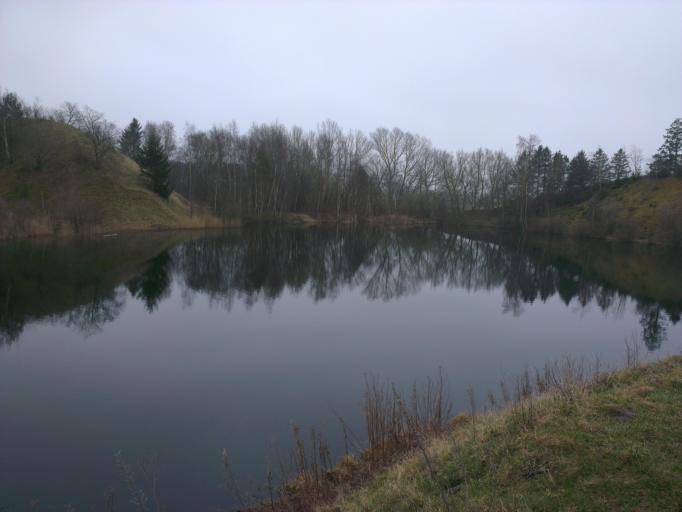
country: DK
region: Capital Region
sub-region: Frederikssund Kommune
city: Skibby
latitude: 55.7659
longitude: 12.0270
